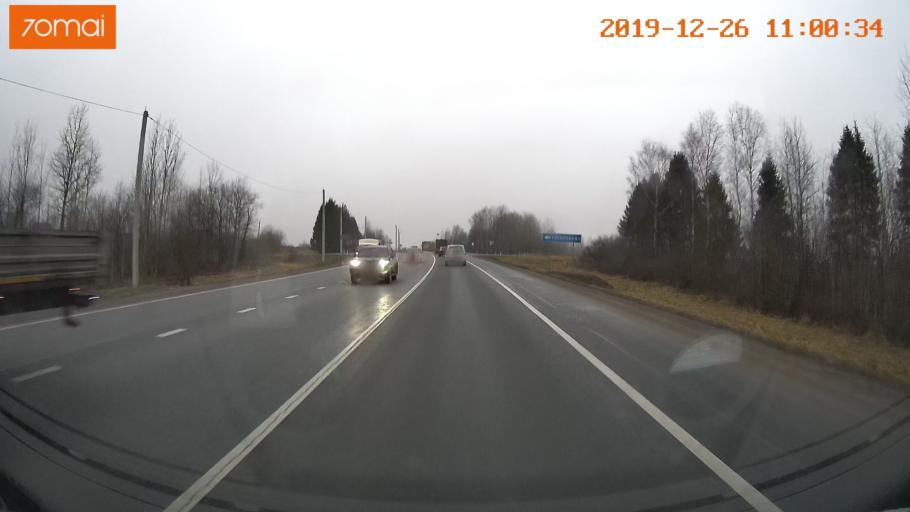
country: RU
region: Vologda
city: Molochnoye
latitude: 59.1673
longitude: 39.4472
